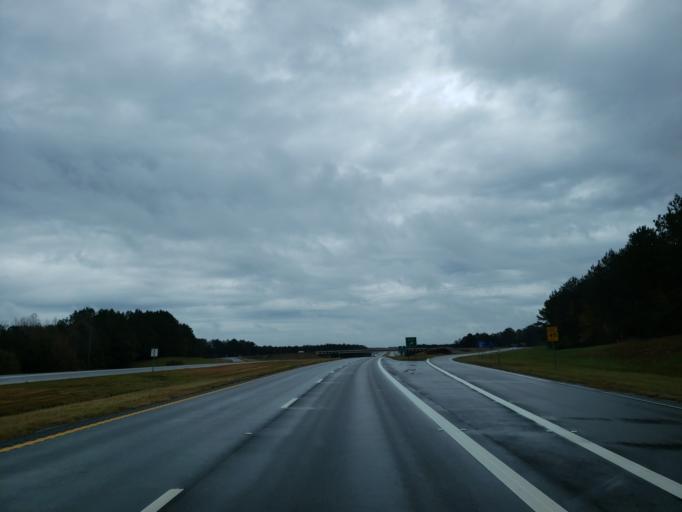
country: US
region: Mississippi
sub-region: Wayne County
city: Waynesboro
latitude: 31.7033
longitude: -88.6489
